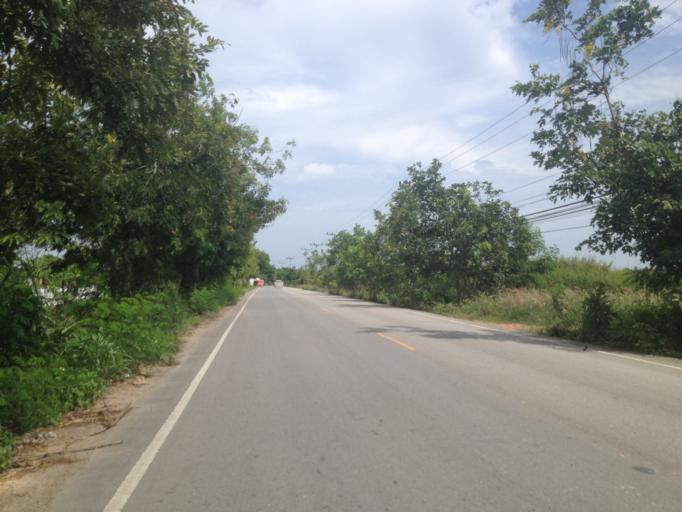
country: TH
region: Chiang Mai
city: Hang Dong
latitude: 18.6863
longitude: 98.9675
